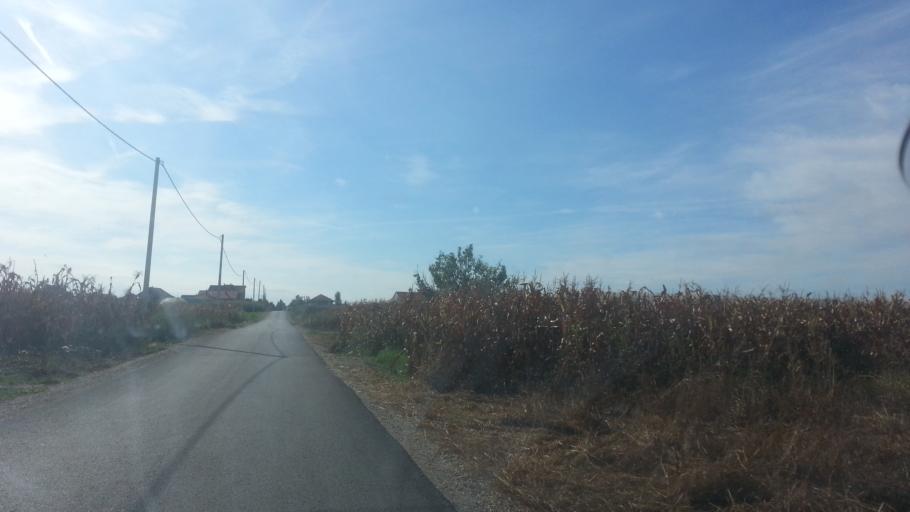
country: RS
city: Stari Banovci
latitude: 44.9758
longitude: 20.2717
